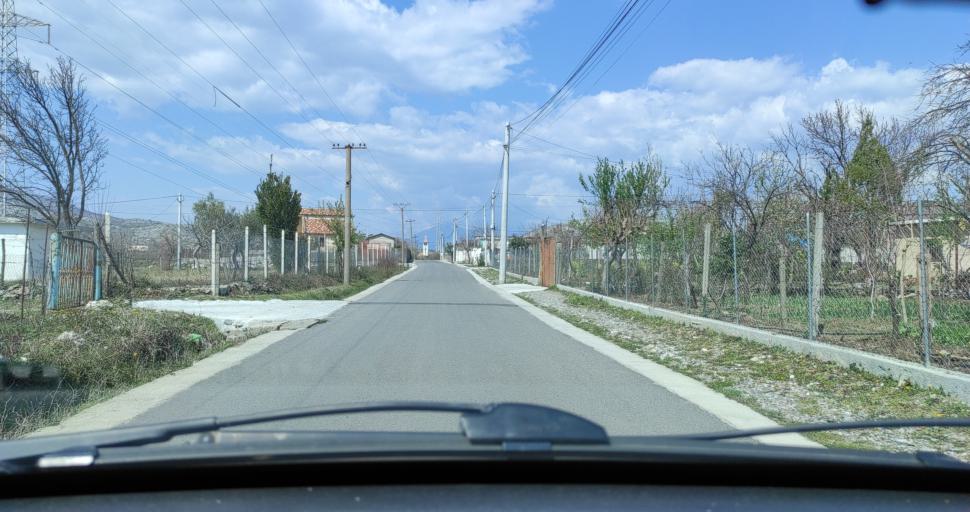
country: AL
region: Shkoder
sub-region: Rrethi i Shkodres
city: Vau i Dejes
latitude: 42.0005
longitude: 19.6426
